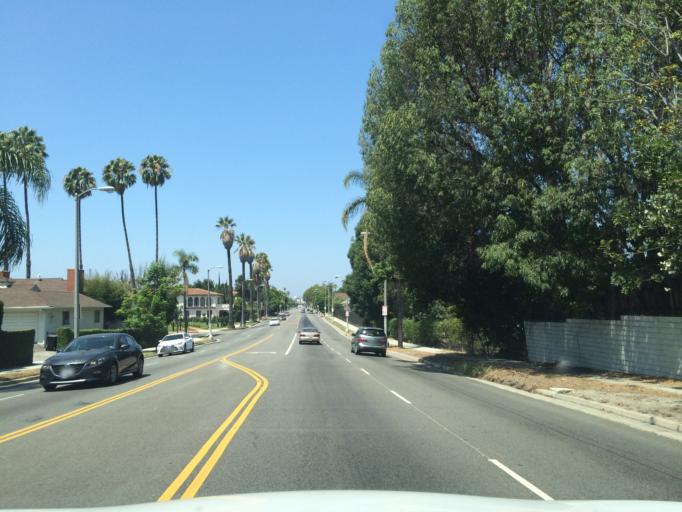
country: US
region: California
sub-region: Los Angeles County
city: Hollywood
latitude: 34.0689
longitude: -118.3310
